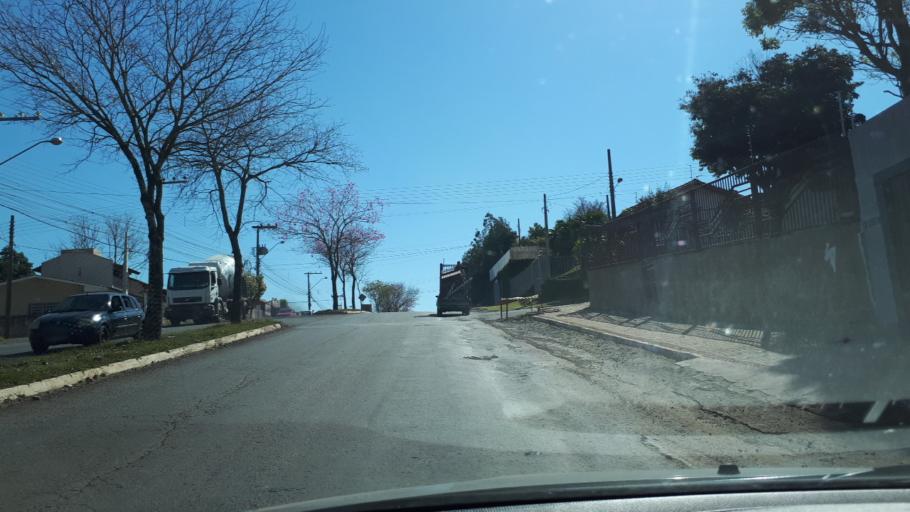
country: BR
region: Santa Catarina
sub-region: Chapeco
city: Chapeco
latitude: -27.1251
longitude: -52.6065
